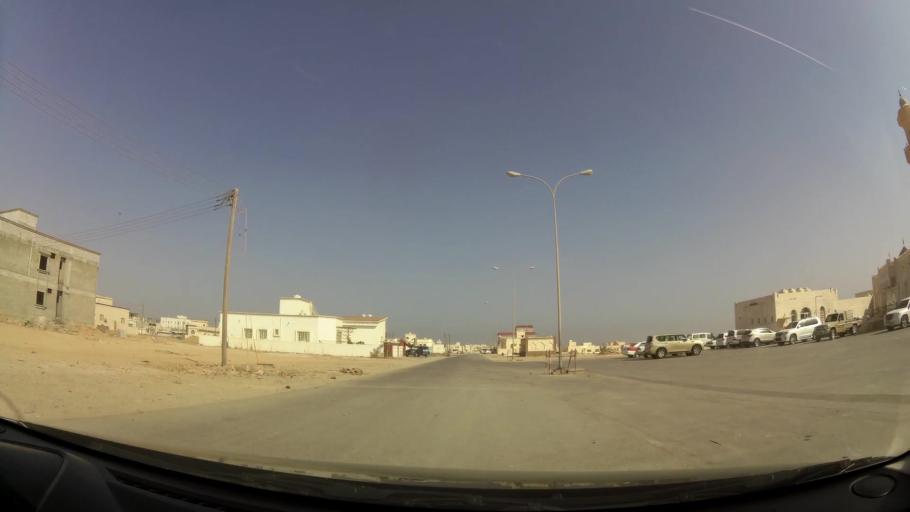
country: OM
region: Zufar
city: Salalah
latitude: 17.0084
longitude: 54.0036
